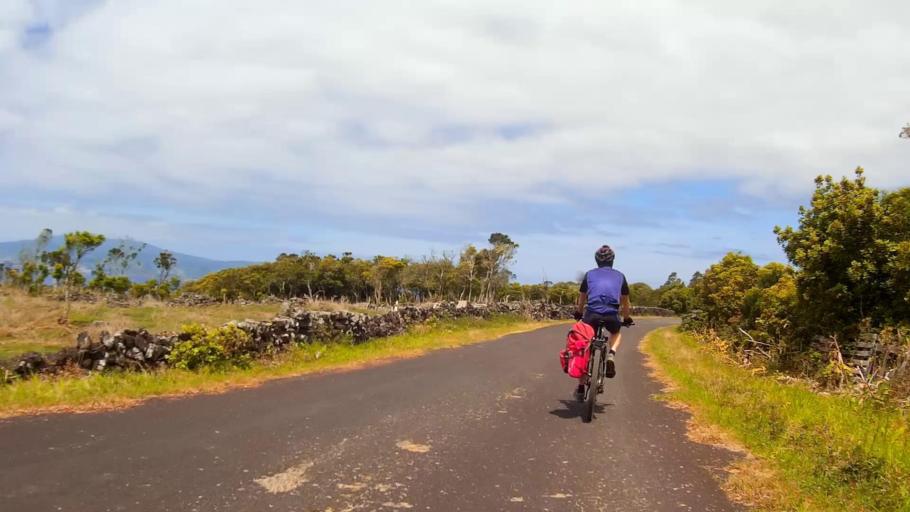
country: PT
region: Azores
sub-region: Madalena
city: Madalena
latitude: 38.4942
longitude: -28.5034
